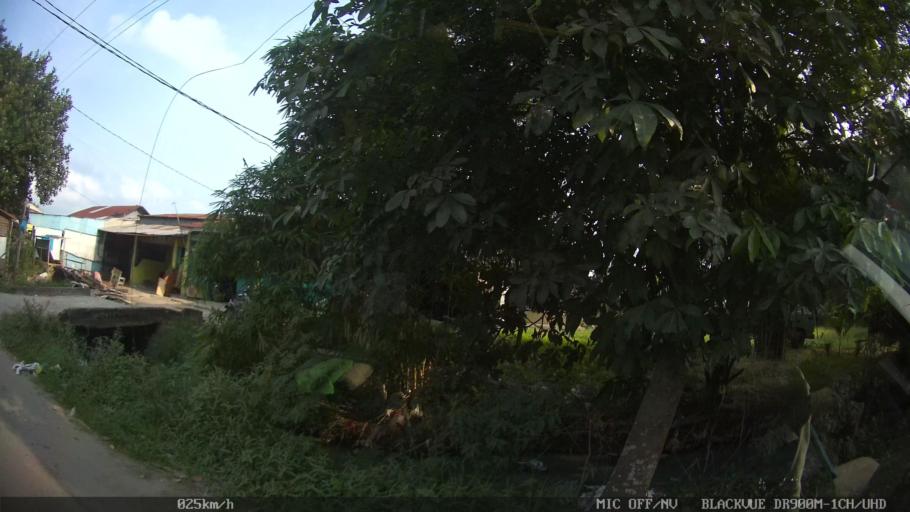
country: ID
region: North Sumatra
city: Medan
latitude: 3.5813
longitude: 98.7514
